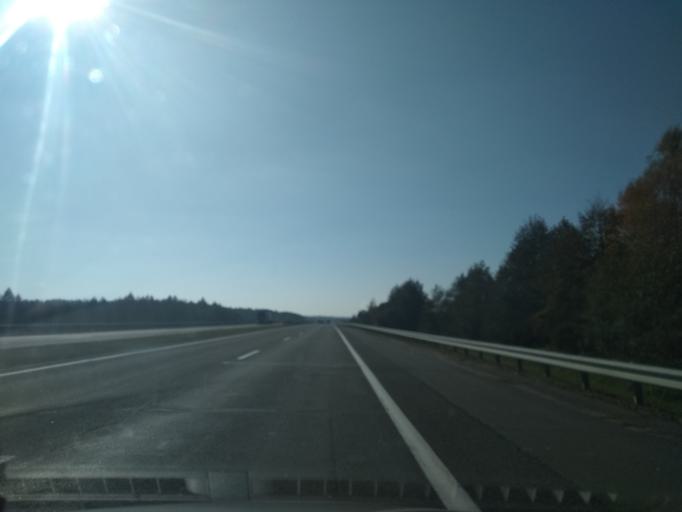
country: BY
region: Brest
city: Ivatsevichy
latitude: 52.7908
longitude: 25.5594
